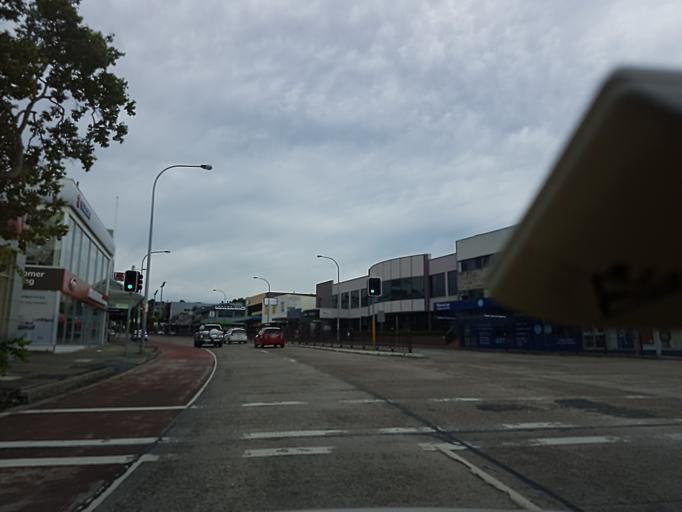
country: AU
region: New South Wales
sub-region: Warringah
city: Brookvale
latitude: -33.7642
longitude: 151.2712
